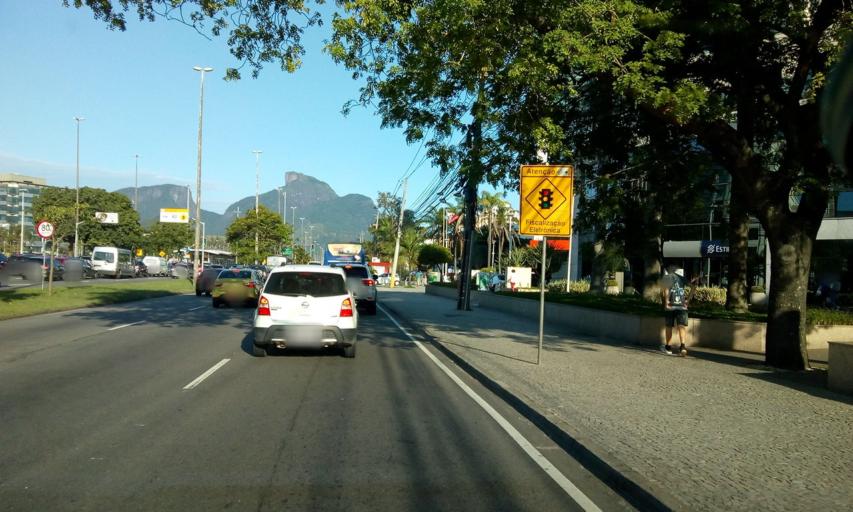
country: BR
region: Rio de Janeiro
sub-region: Rio De Janeiro
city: Rio de Janeiro
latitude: -23.0005
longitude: -43.3489
